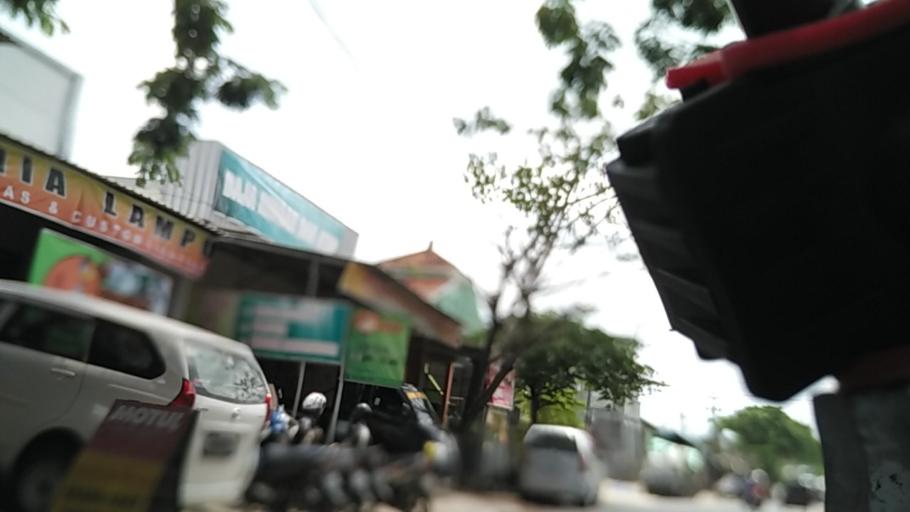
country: ID
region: Central Java
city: Semarang
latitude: -7.0181
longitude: 110.3381
